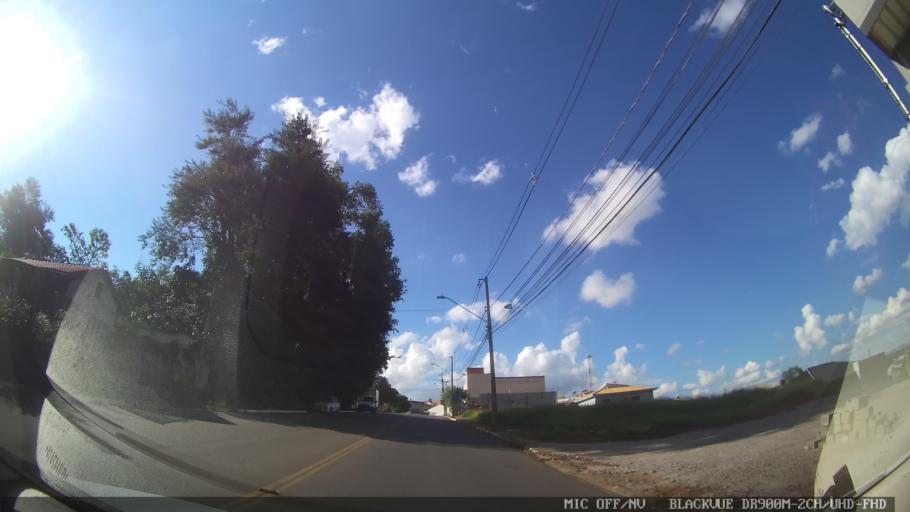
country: BR
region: Minas Gerais
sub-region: Extrema
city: Extrema
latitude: -22.8525
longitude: -46.3296
